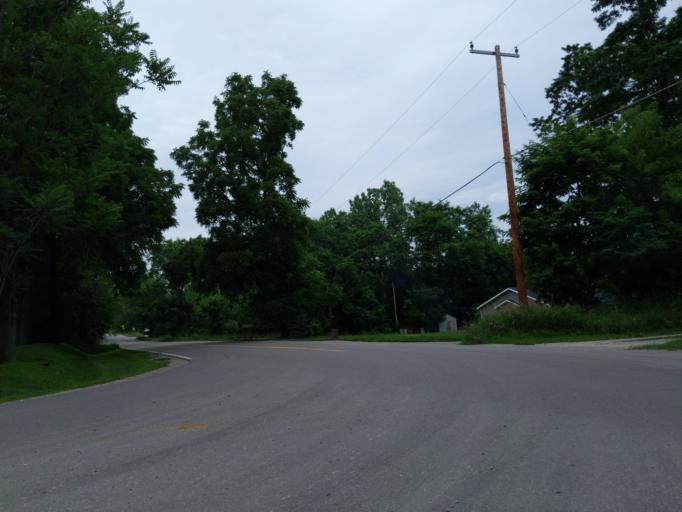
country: US
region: Michigan
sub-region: Livingston County
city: Whitmore Lake
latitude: 42.4423
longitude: -83.7930
